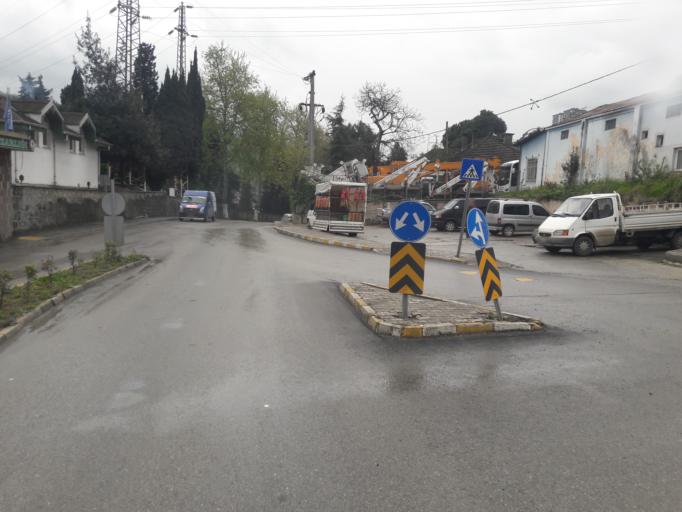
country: TR
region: Trabzon
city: Trabzon
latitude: 40.9944
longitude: 39.7496
